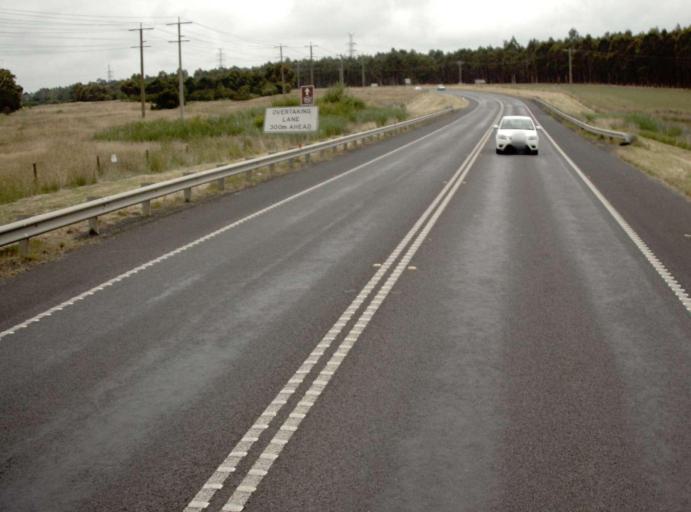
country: AU
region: Victoria
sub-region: Latrobe
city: Morwell
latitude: -38.2782
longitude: 146.4162
